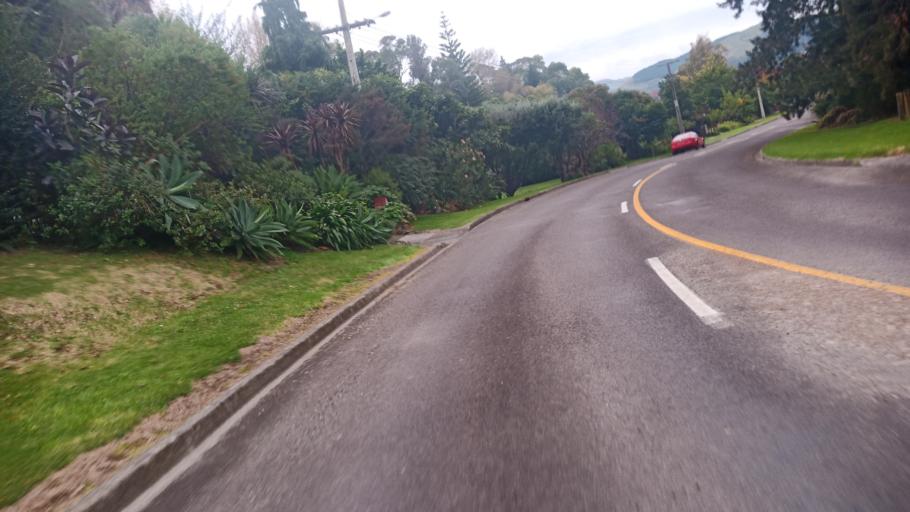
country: NZ
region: Gisborne
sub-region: Gisborne District
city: Gisborne
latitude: -38.6808
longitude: 178.0396
